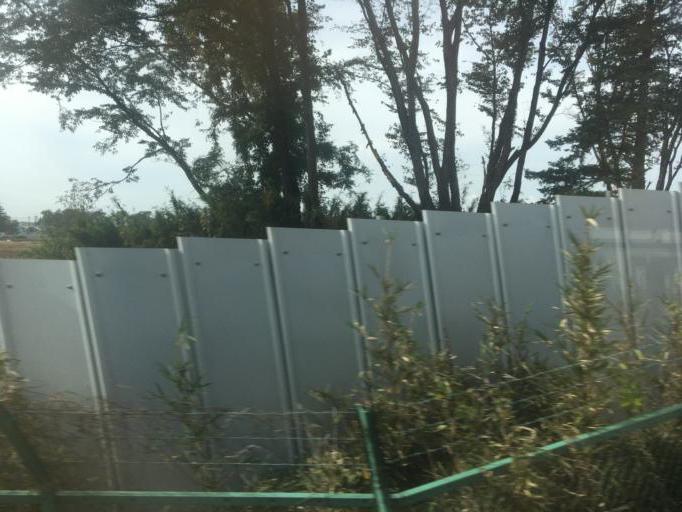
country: JP
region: Saitama
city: Sayama
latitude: 35.8376
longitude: 139.4068
